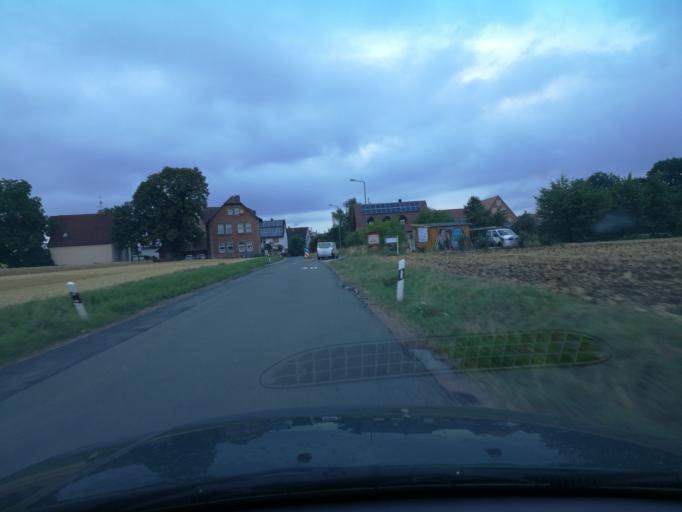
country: DE
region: Bavaria
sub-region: Regierungsbezirk Mittelfranken
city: Obermichelbach
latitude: 49.5375
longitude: 10.9597
